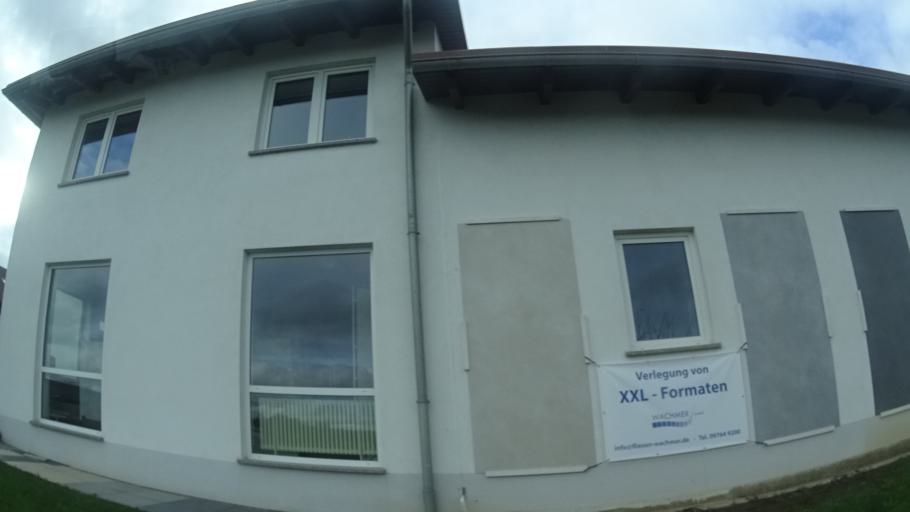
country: DE
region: Bavaria
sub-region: Regierungsbezirk Unterfranken
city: Hochheim
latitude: 50.3668
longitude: 10.4701
